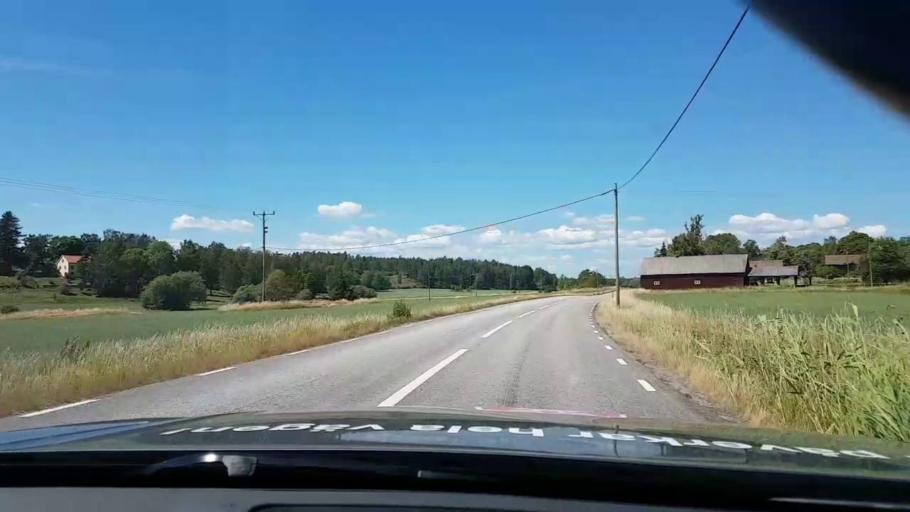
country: SE
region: Kalmar
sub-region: Vasterviks Kommun
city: Forserum
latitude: 57.9330
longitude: 16.5090
